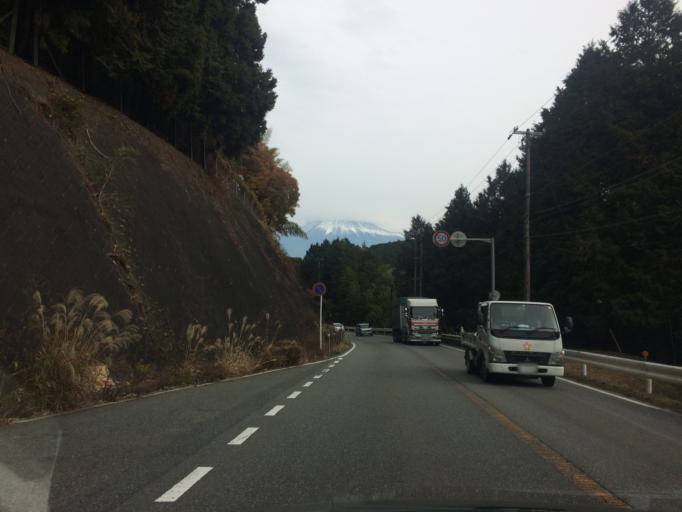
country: JP
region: Shizuoka
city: Fujinomiya
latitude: 35.1800
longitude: 138.5244
